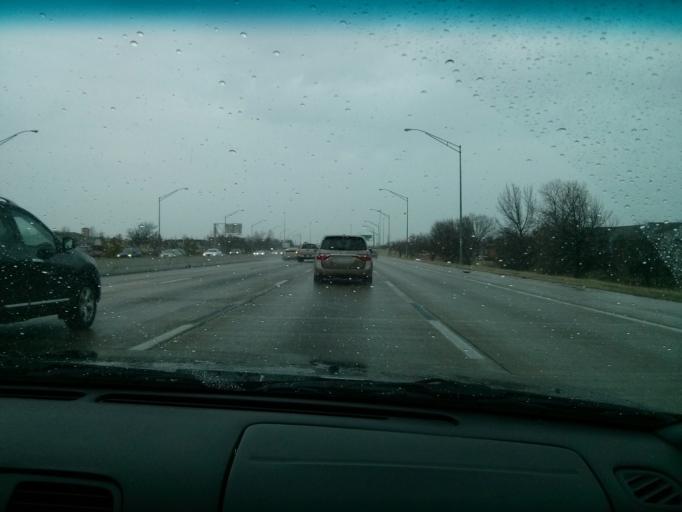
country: US
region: Oklahoma
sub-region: Tulsa County
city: Broken Arrow
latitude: 36.0685
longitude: -95.8593
